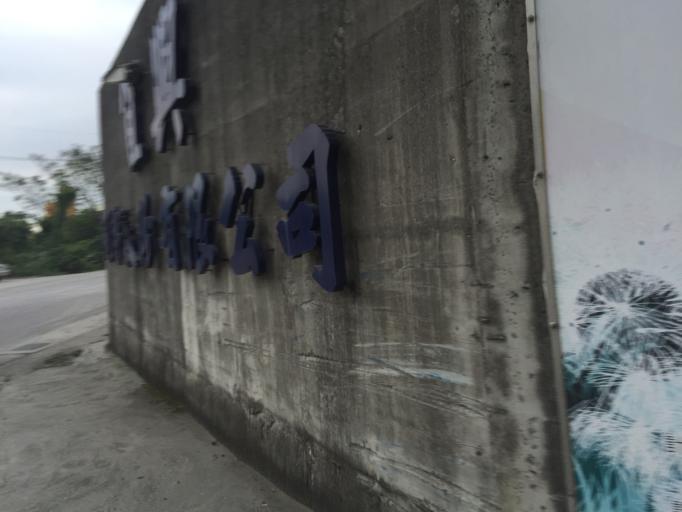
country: TW
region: Taiwan
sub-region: Yilan
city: Yilan
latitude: 24.7809
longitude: 121.7323
